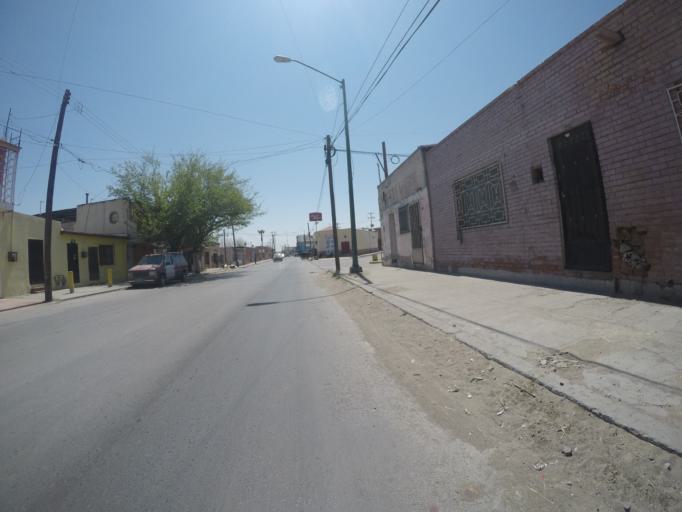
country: MX
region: Chihuahua
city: Ciudad Juarez
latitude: 31.7318
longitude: -106.4846
